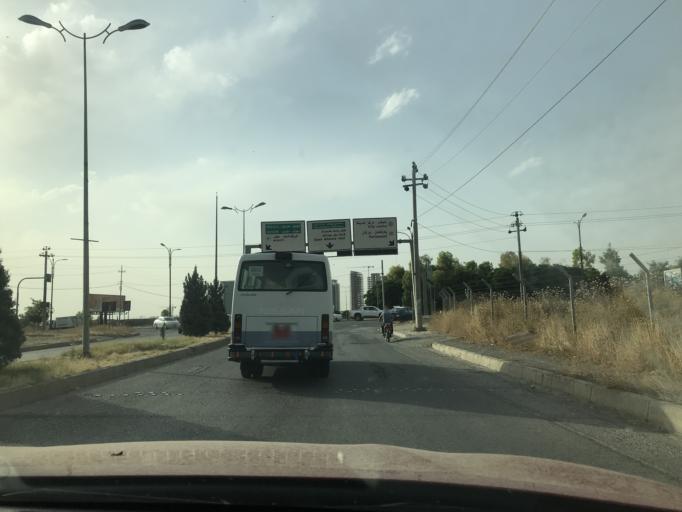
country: IQ
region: Arbil
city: Erbil
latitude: 36.1818
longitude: 43.9756
